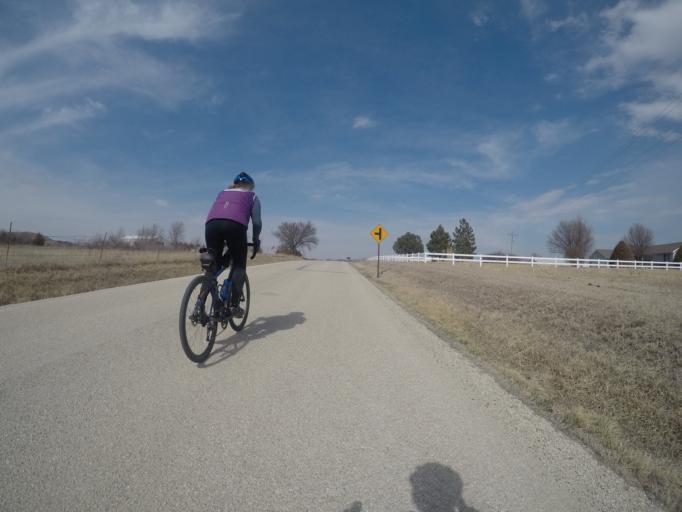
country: US
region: Kansas
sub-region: Geary County
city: Grandview Plaza
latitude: 39.0138
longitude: -96.7456
